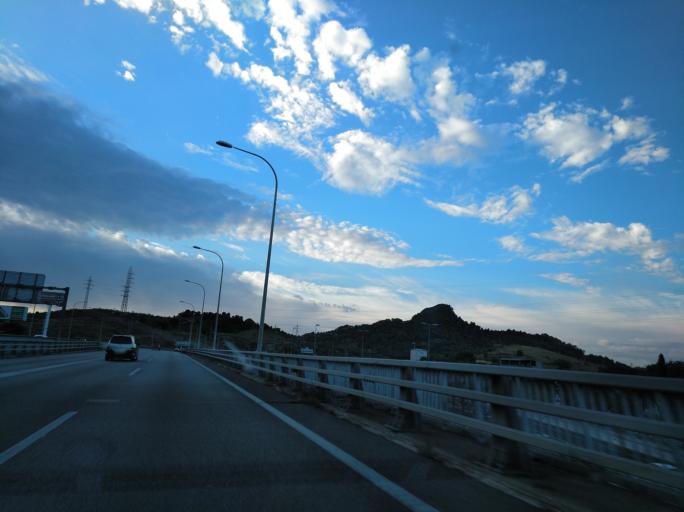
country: ES
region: Catalonia
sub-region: Provincia de Barcelona
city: Montcada i Reixac
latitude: 41.4642
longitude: 2.1799
